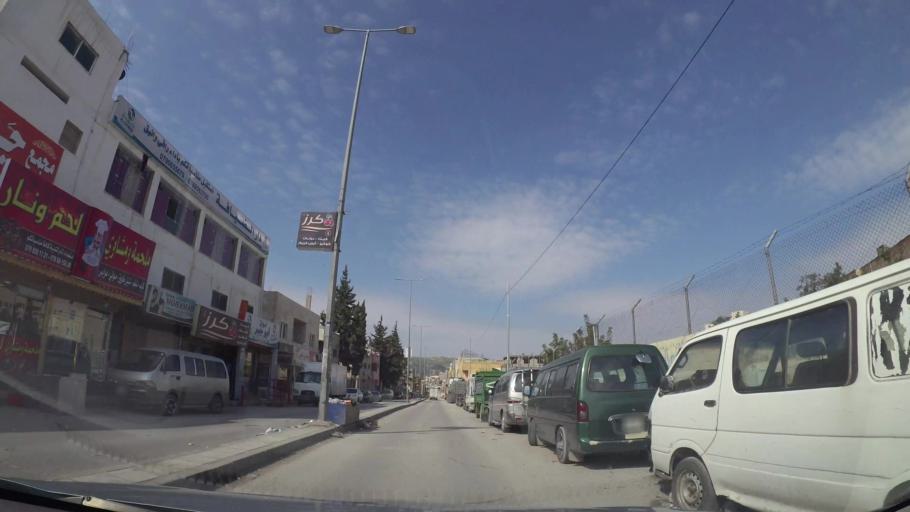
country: JO
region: Amman
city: Al Jubayhah
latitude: 32.0776
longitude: 35.8436
